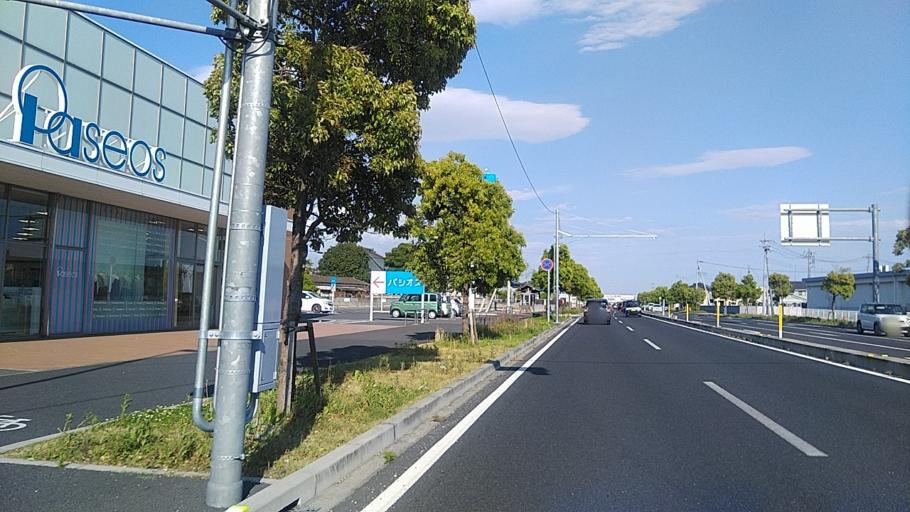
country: JP
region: Gunma
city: Ota
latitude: 36.2687
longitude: 139.3823
